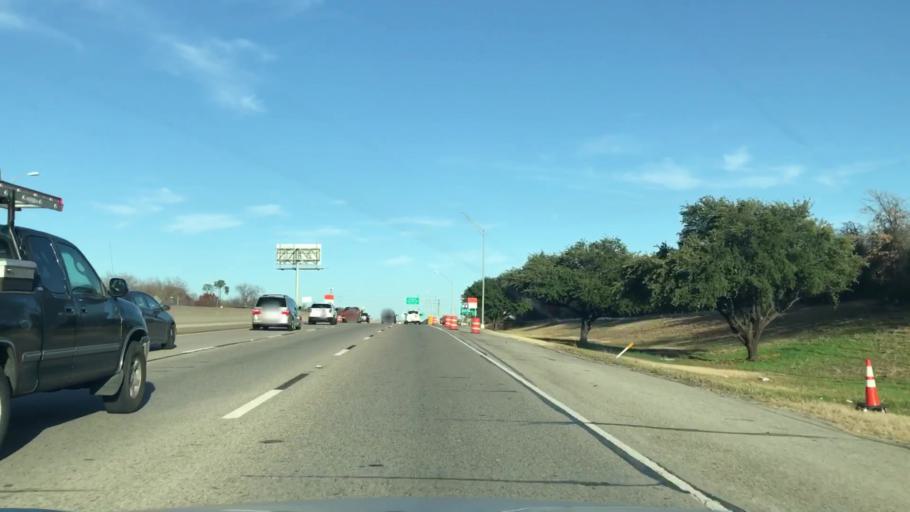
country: US
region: Texas
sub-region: Tarrant County
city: Richland Hills
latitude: 32.7969
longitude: -97.2310
